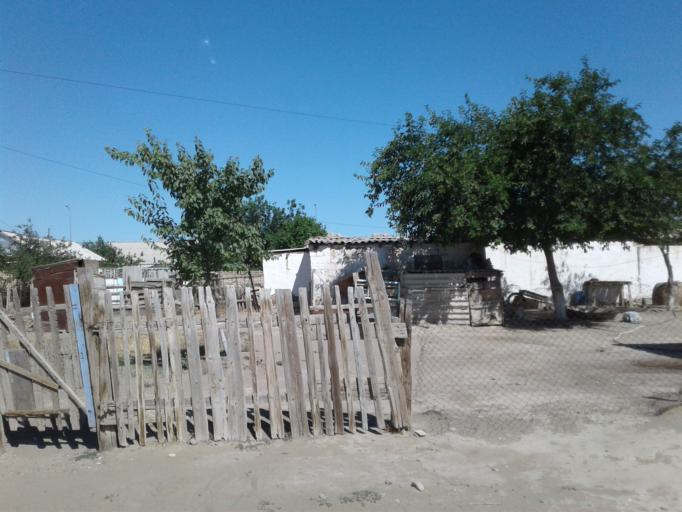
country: TM
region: Mary
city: Bayramaly
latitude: 38.0895
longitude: 62.7977
